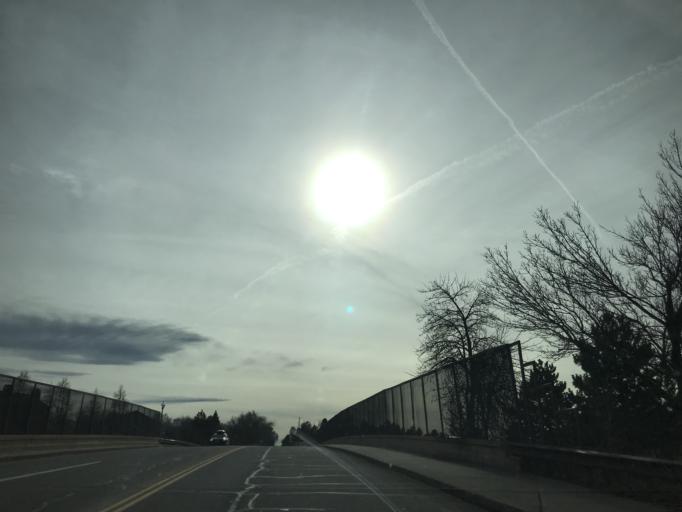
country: US
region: Colorado
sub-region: Arapahoe County
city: Littleton
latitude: 39.6098
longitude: -105.0163
